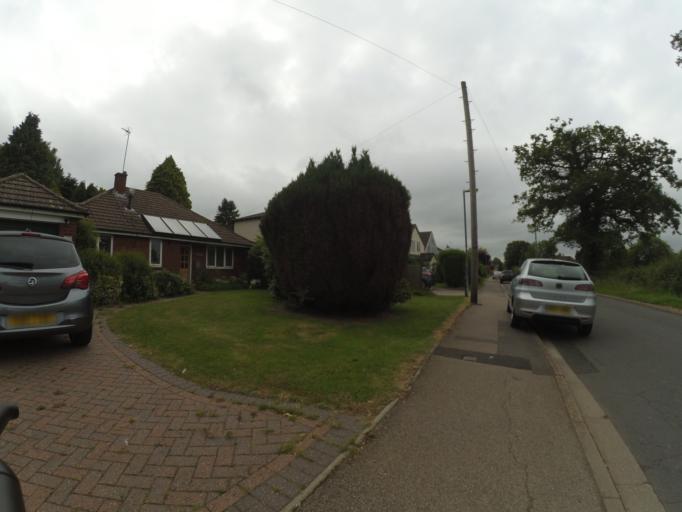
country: GB
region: England
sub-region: Warwickshire
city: Dunchurch
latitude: 52.3423
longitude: -1.2920
